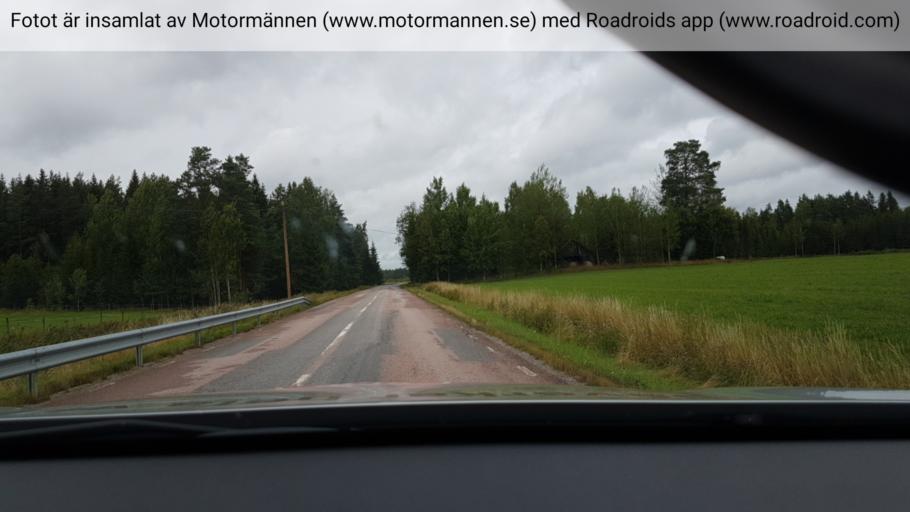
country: SE
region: Uppsala
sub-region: Heby Kommun
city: Tarnsjo
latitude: 60.1793
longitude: 17.0356
